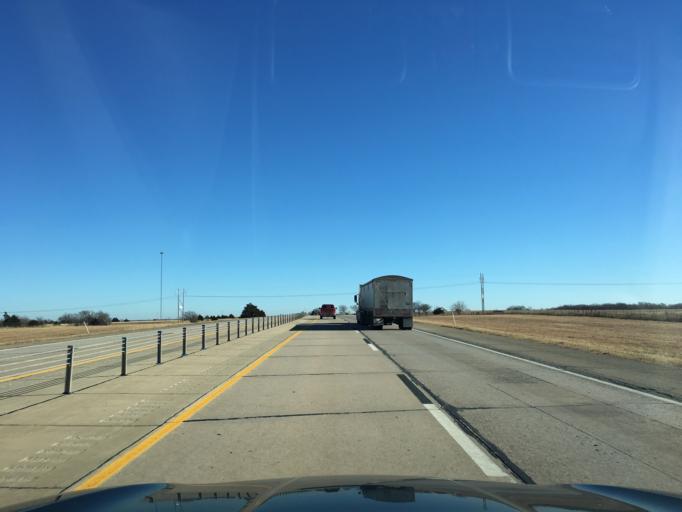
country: US
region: Oklahoma
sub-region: Pawnee County
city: Pawnee
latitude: 36.2257
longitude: -96.8987
